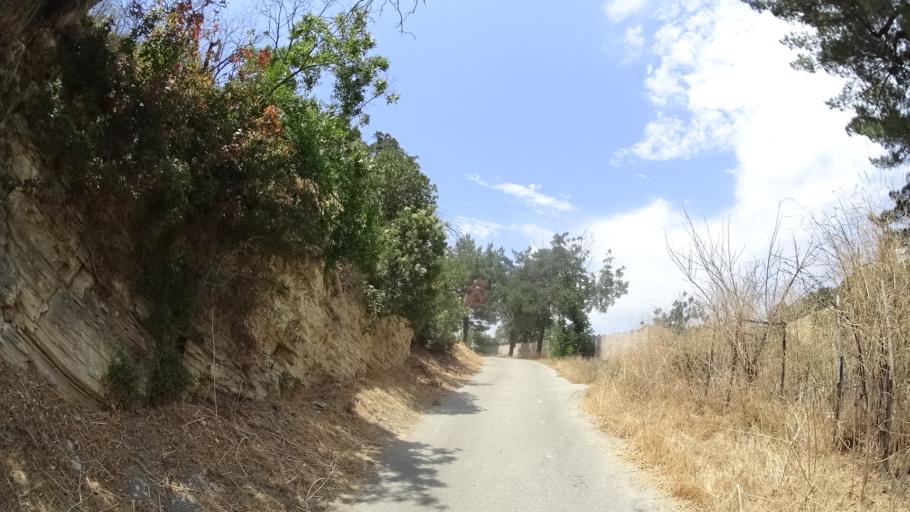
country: US
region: California
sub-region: Los Angeles County
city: Sherman Oaks
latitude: 34.1377
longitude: -118.4268
